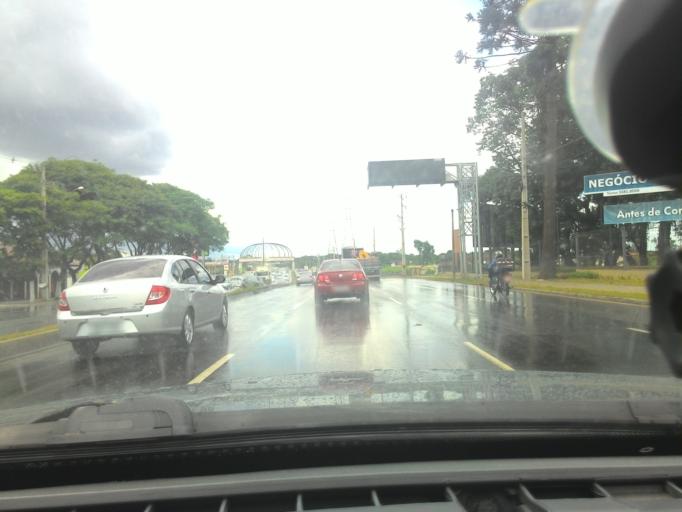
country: BR
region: Parana
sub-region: Sao Jose Dos Pinhais
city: Sao Jose dos Pinhais
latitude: -25.5168
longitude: -49.2003
